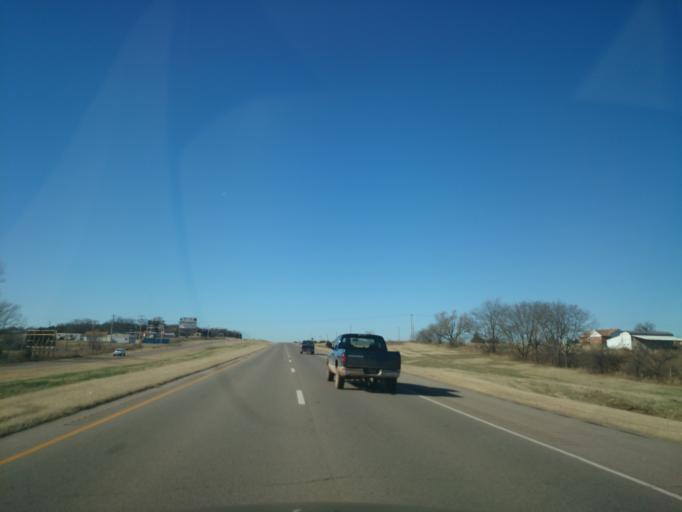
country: US
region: Oklahoma
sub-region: Payne County
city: Stillwater
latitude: 36.1162
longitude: -97.1557
